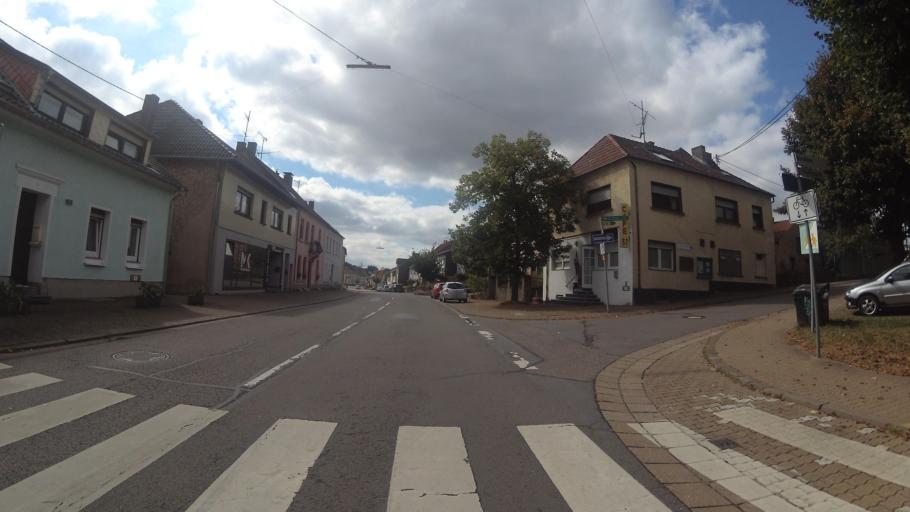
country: FR
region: Lorraine
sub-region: Departement de la Moselle
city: Carling
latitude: 49.1827
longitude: 6.7422
